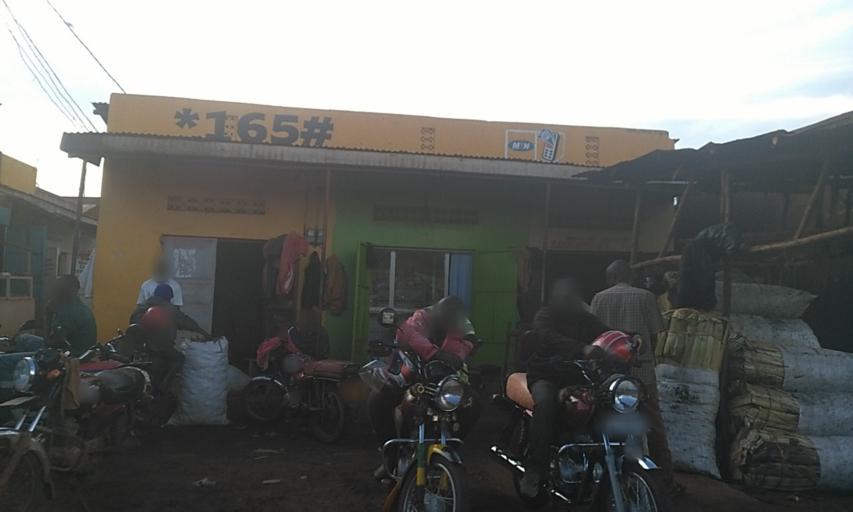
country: UG
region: Central Region
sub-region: Wakiso District
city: Kajansi
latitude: 0.2563
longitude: 32.5071
